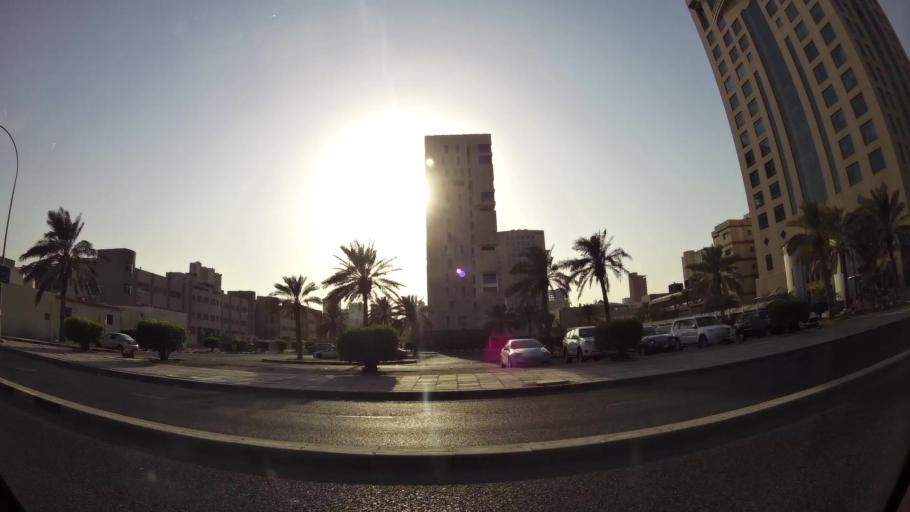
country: KW
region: Muhafazat Hawalli
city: As Salimiyah
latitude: 29.3413
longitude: 48.0781
